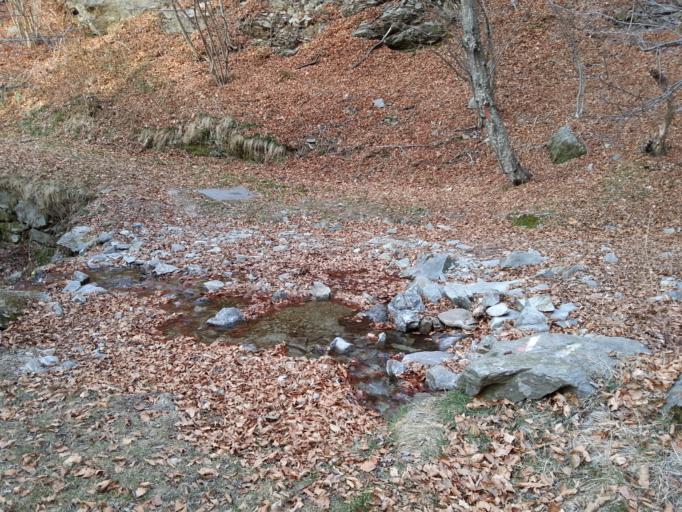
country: CH
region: Ticino
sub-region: Lugano District
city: Gravesano
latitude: 46.0658
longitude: 8.8802
